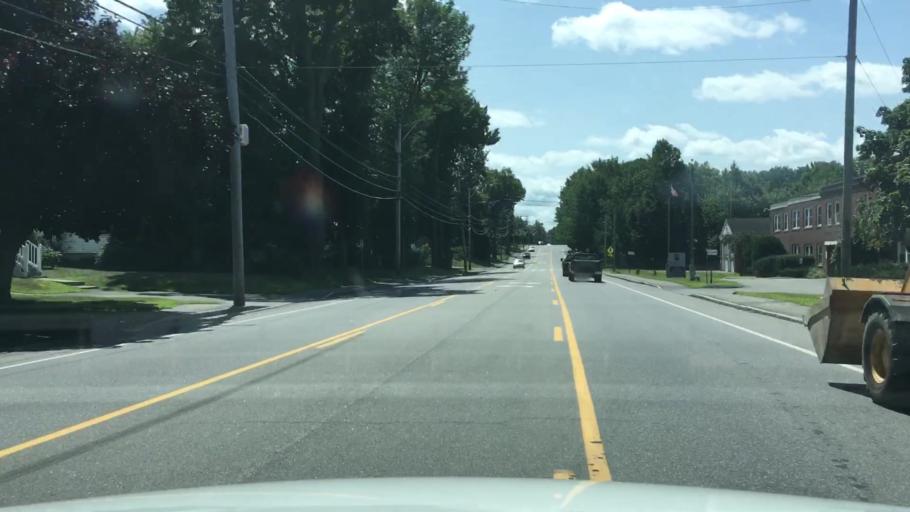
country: US
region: Maine
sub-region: Kennebec County
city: Augusta
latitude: 44.3080
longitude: -69.7651
